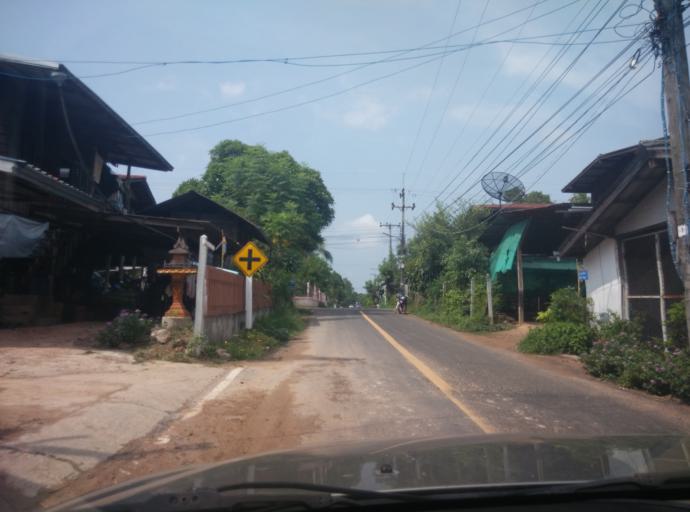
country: TH
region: Sisaket
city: Huai Thap Than
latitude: 15.0286
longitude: 104.0742
